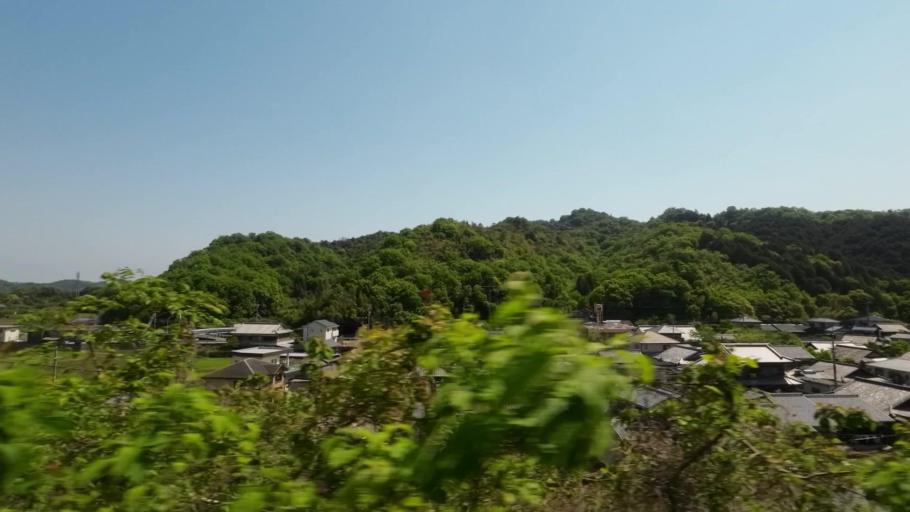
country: JP
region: Ehime
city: Niihama
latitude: 33.9708
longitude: 133.3560
